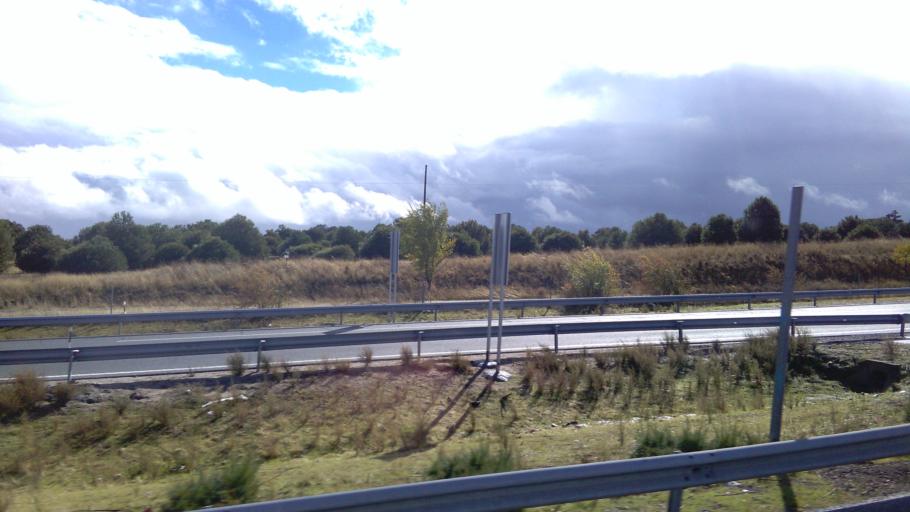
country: ES
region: Madrid
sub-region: Provincia de Madrid
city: Navalcarnero
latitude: 40.2527
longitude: -4.0517
